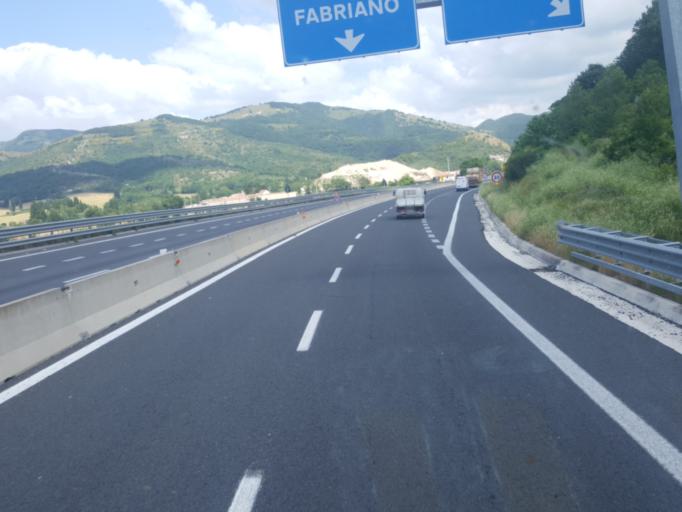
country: IT
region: Umbria
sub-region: Provincia di Perugia
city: Fossato di Vico
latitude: 43.2997
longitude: 12.7505
